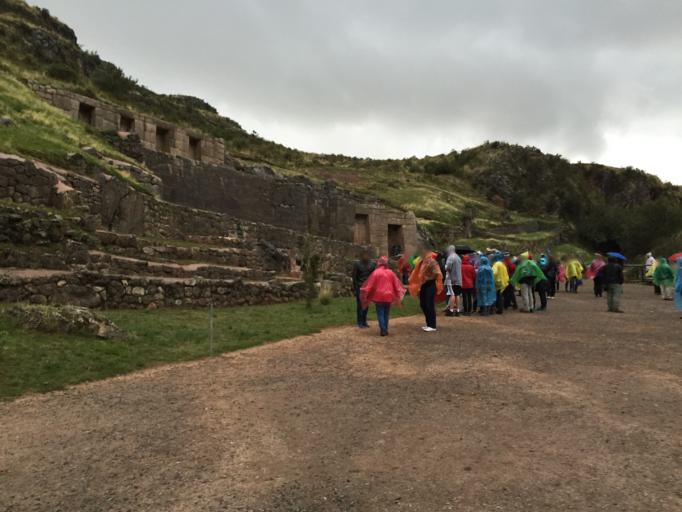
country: PE
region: Cusco
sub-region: Provincia de Cusco
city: Cusco
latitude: -13.4790
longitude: -71.9671
